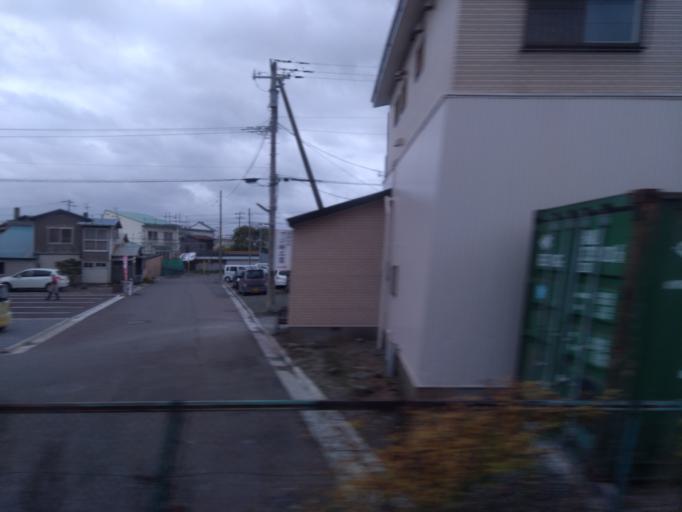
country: JP
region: Hokkaido
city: Hakodate
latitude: 41.7880
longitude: 140.7299
